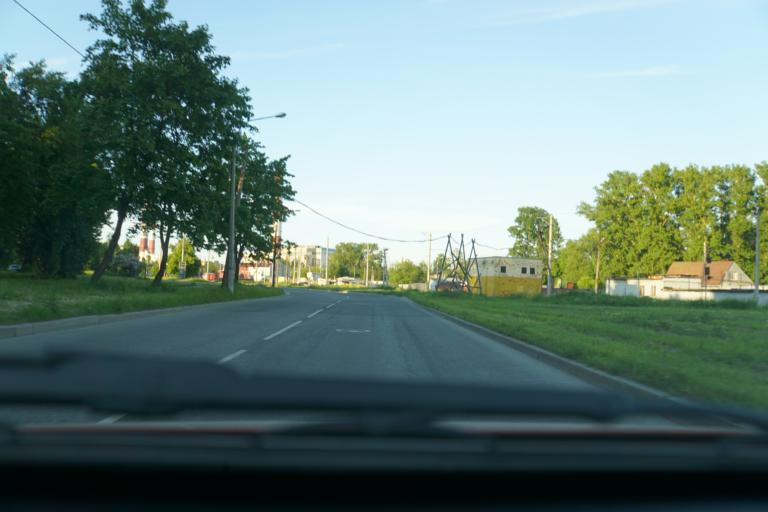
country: RU
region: St.-Petersburg
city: Avtovo
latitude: 59.8626
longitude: 30.2844
